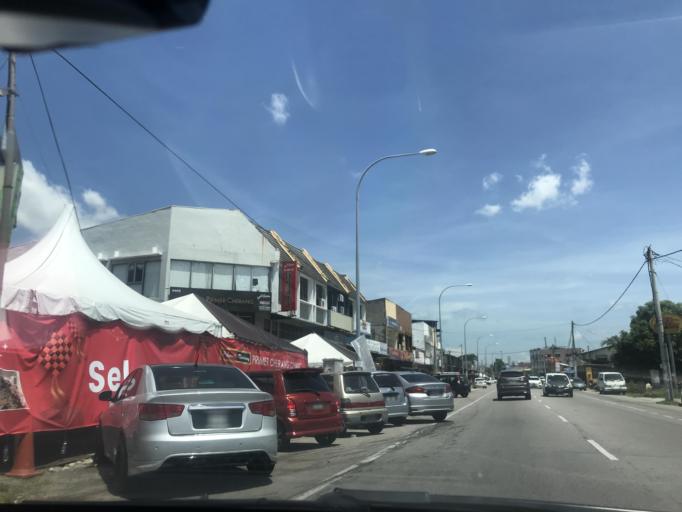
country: MY
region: Kelantan
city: Kota Bharu
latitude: 6.1245
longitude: 102.2648
